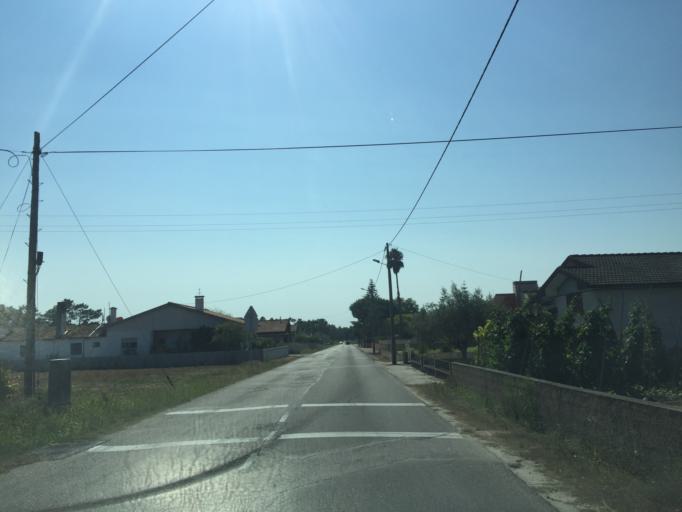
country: PT
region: Coimbra
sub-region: Montemor-O-Velho
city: Arazede
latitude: 40.3172
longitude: -8.7315
